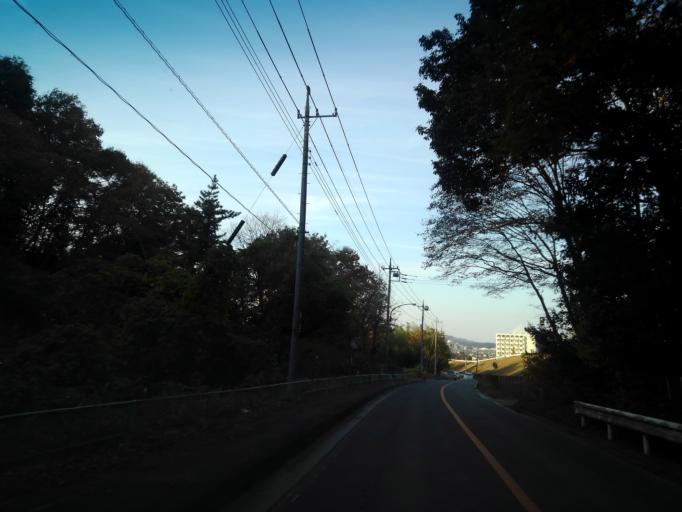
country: JP
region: Saitama
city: Hanno
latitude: 35.8294
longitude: 139.3384
